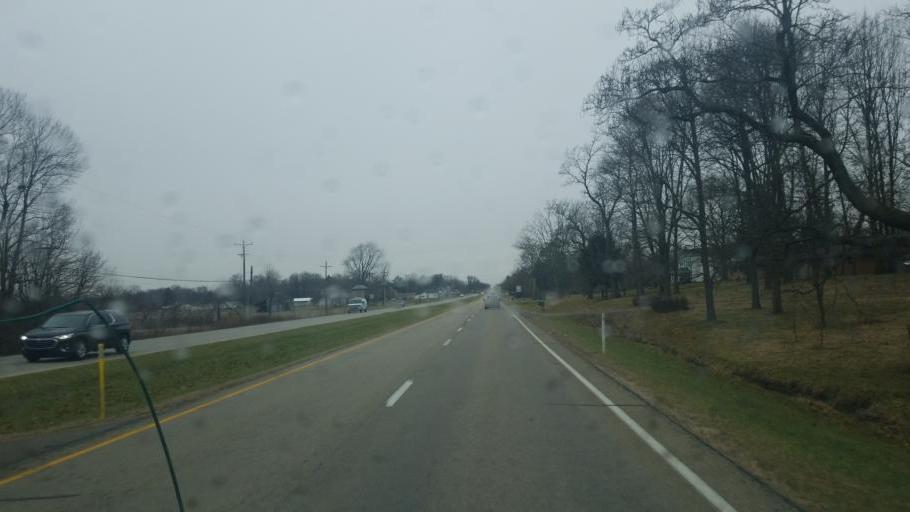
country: US
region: Indiana
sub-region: Henry County
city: Knightstown
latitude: 39.7917
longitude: -85.6050
